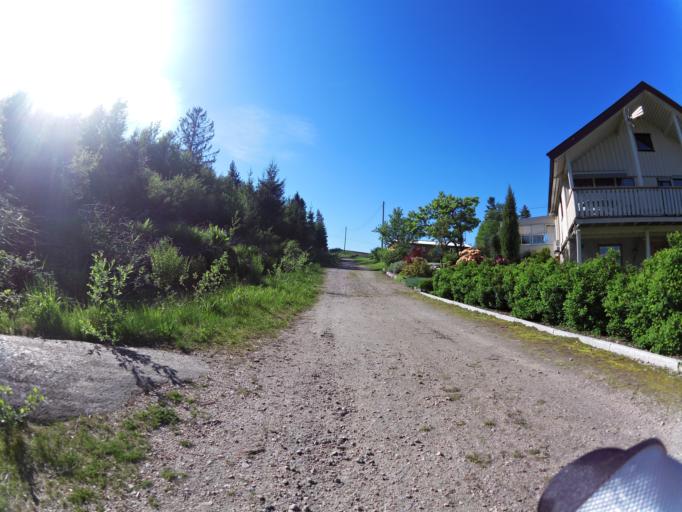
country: NO
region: Ostfold
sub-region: Sarpsborg
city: Sarpsborg
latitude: 59.2228
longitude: 11.0547
